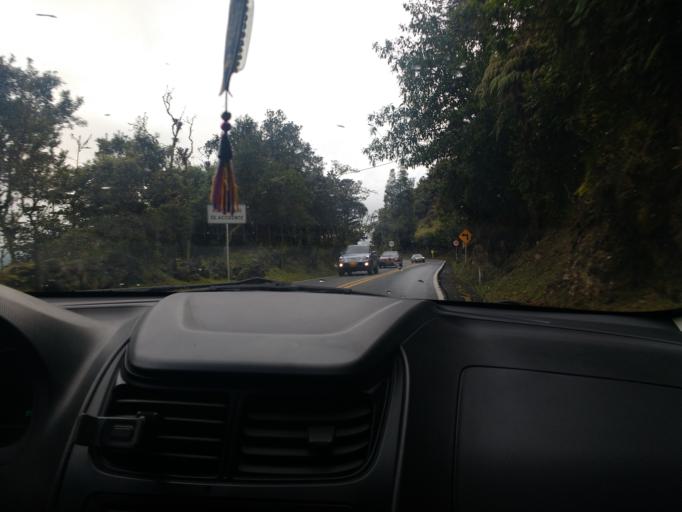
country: CO
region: Cundinamarca
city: Choachi
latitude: 4.5655
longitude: -73.9593
